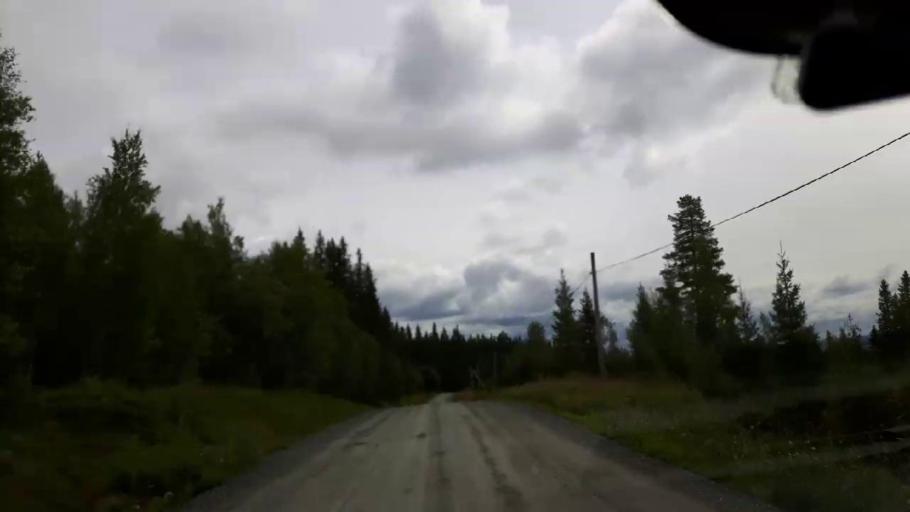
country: SE
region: Jaemtland
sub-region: Krokoms Kommun
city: Valla
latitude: 63.6796
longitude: 13.9277
